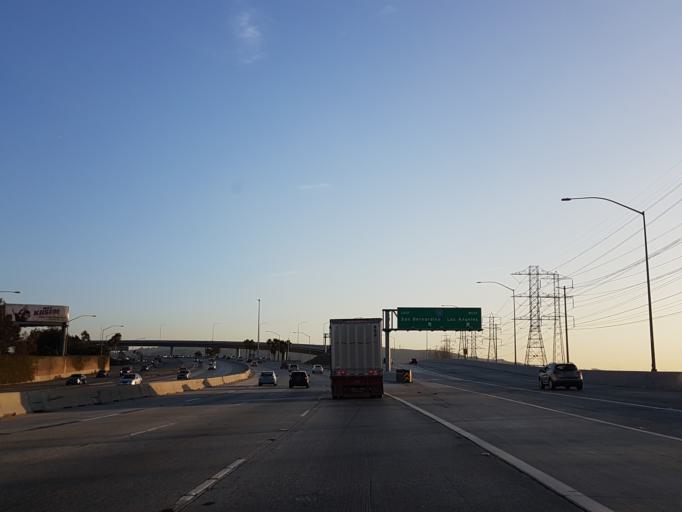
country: US
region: California
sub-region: Los Angeles County
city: El Monte
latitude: 34.0702
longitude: -118.0005
